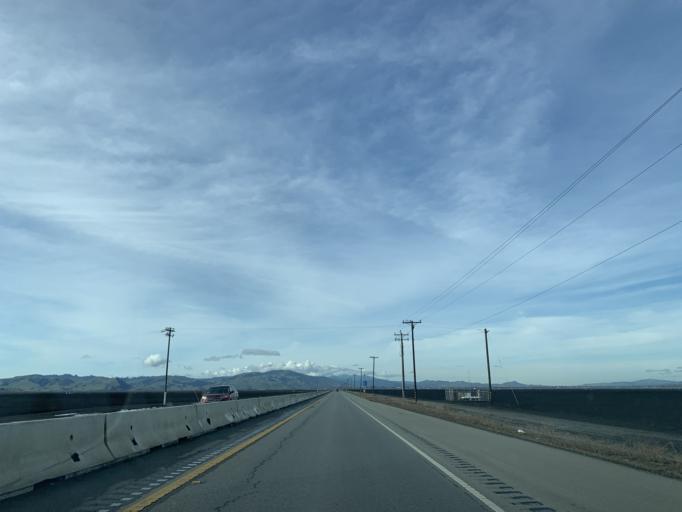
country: US
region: California
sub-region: San Benito County
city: Hollister
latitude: 36.9205
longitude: -121.4531
